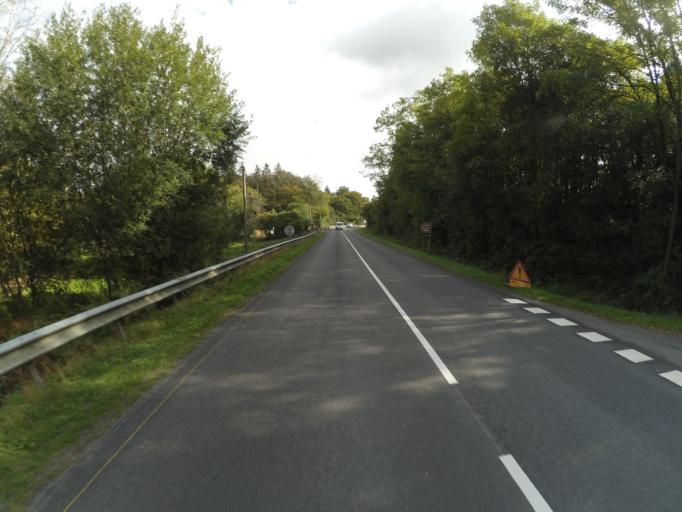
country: FR
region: Pays de la Loire
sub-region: Departement de la Loire-Atlantique
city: Fegreac
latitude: 47.5982
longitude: -2.0143
